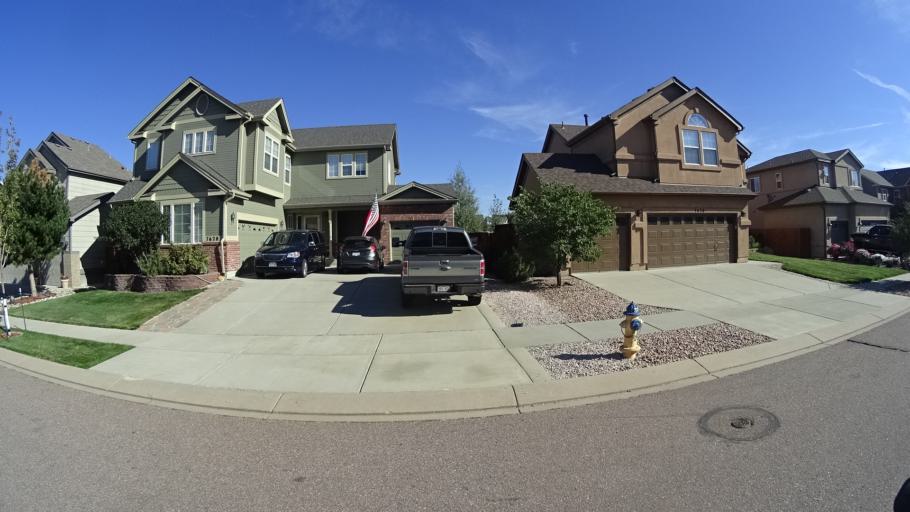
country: US
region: Colorado
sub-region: El Paso County
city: Black Forest
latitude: 38.9436
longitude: -104.7369
